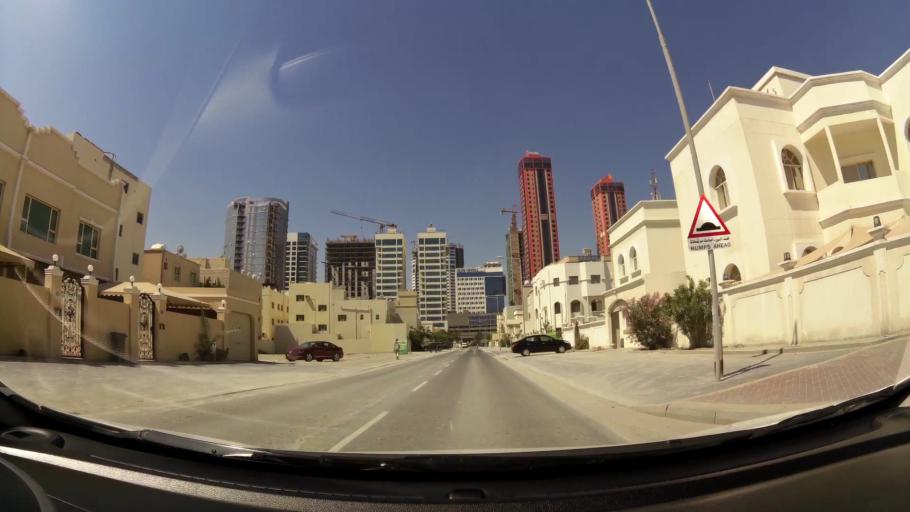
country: BH
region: Manama
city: Manama
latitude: 26.2154
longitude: 50.6145
